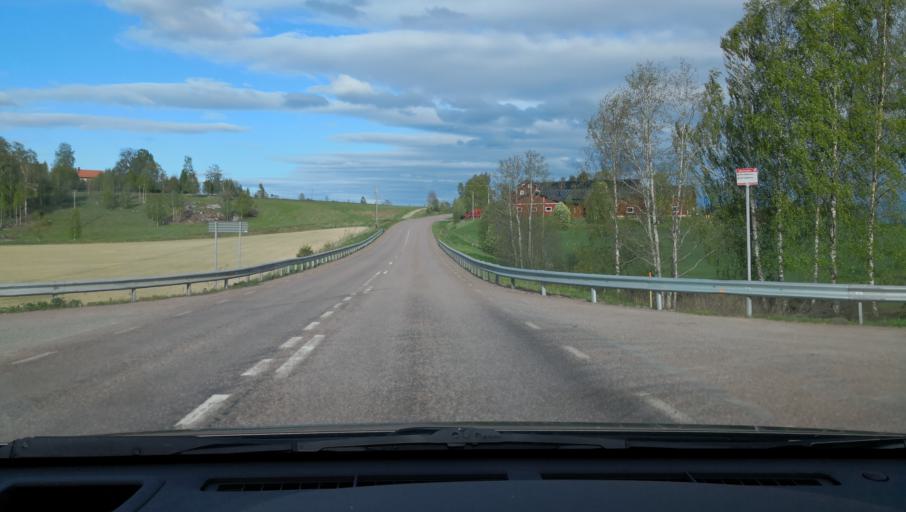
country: SE
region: Dalarna
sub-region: Hedemora Kommun
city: Hedemora
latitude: 60.2845
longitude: 15.9339
